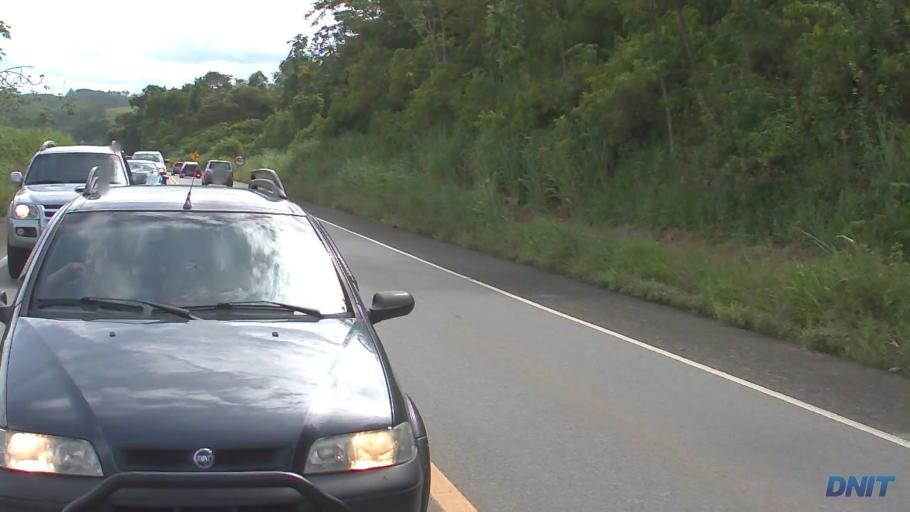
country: BR
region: Minas Gerais
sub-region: Ipaba
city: Ipaba
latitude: -19.3743
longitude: -42.4616
